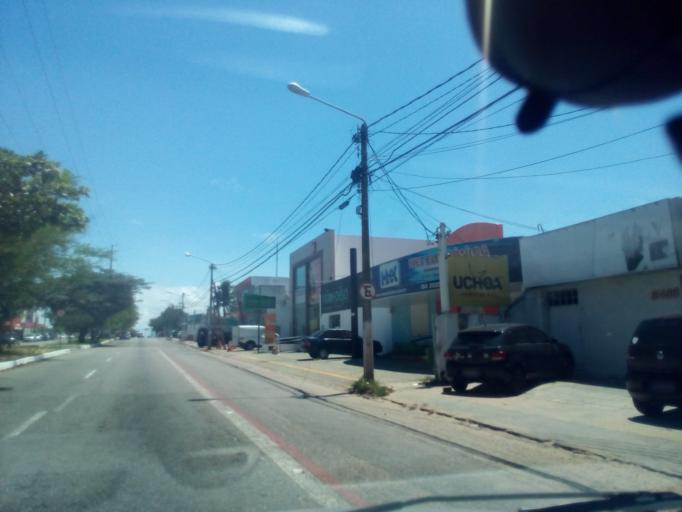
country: BR
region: Rio Grande do Norte
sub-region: Natal
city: Natal
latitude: -5.8378
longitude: -35.2198
